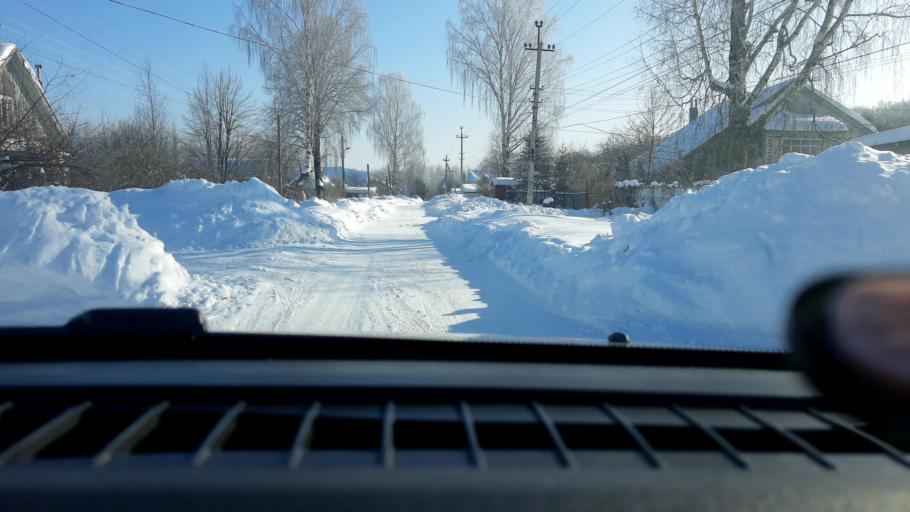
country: RU
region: Nizjnij Novgorod
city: Afonino
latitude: 56.1986
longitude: 44.0373
